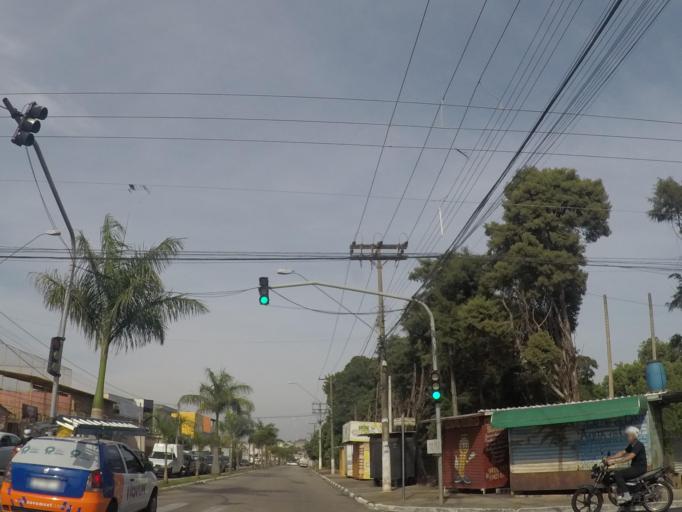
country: BR
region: Sao Paulo
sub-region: Hortolandia
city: Hortolandia
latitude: -22.8531
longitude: -47.1811
